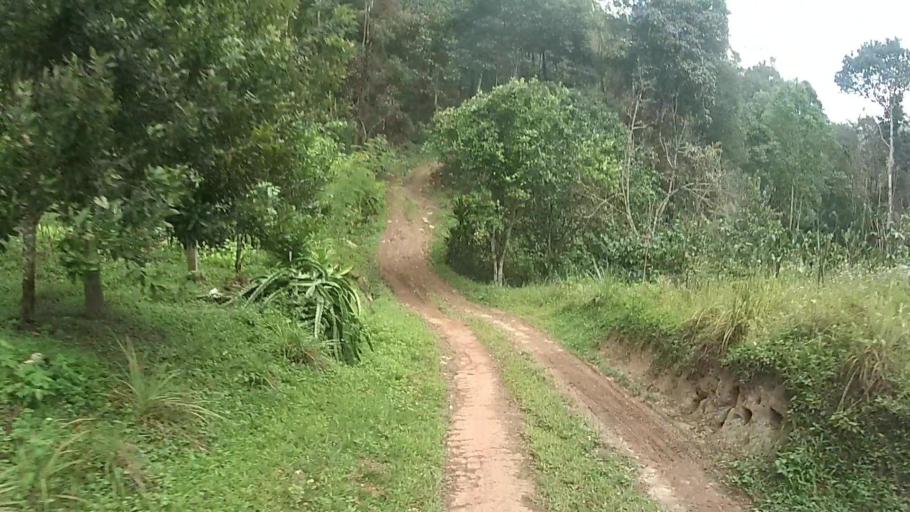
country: TH
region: Lampang
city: Mueang Pan
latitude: 18.9805
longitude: 99.4396
